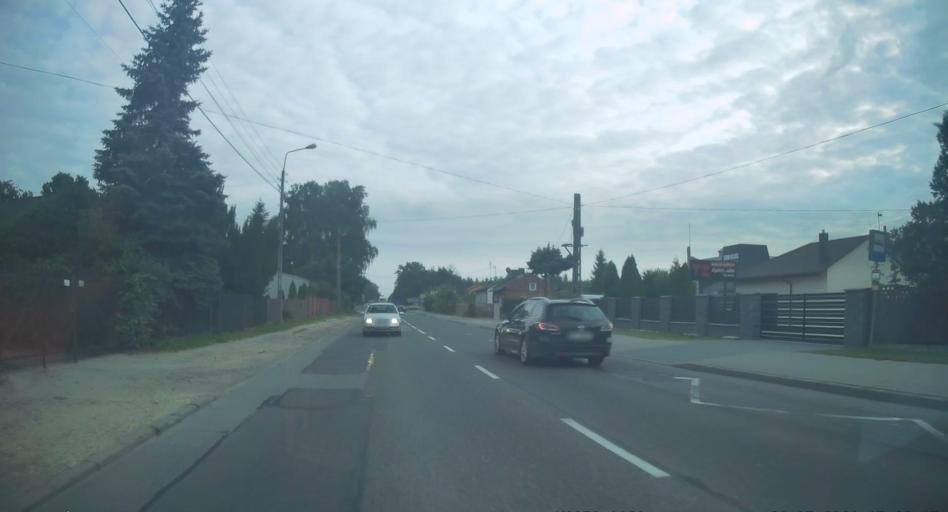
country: PL
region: Lodz Voivodeship
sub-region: Powiat radomszczanski
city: Radomsko
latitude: 51.0452
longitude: 19.4383
